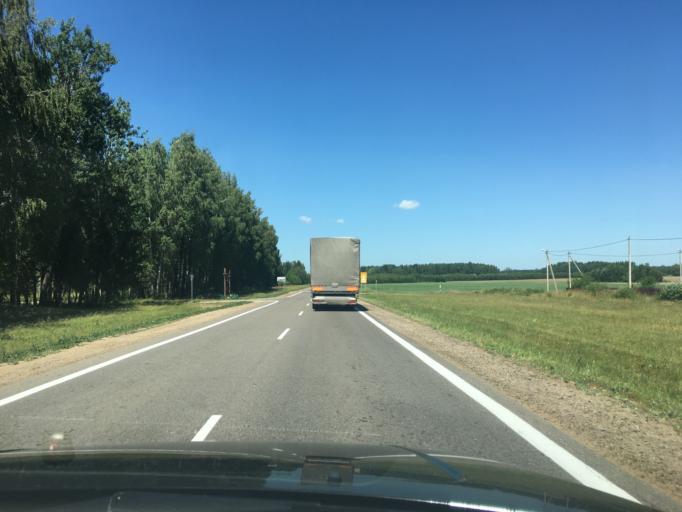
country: BY
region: Grodnenskaya
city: Iwye
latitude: 54.0383
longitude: 25.9197
